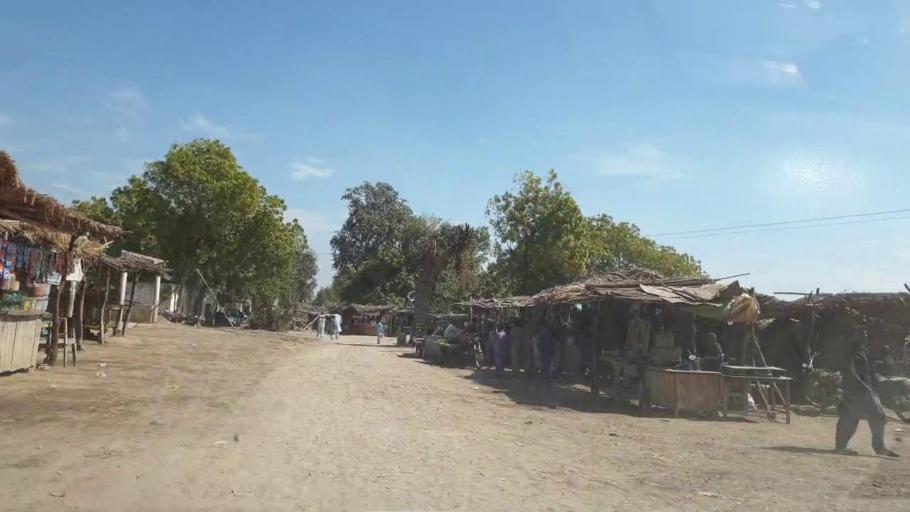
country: PK
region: Sindh
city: Pithoro
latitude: 25.6071
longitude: 69.2148
